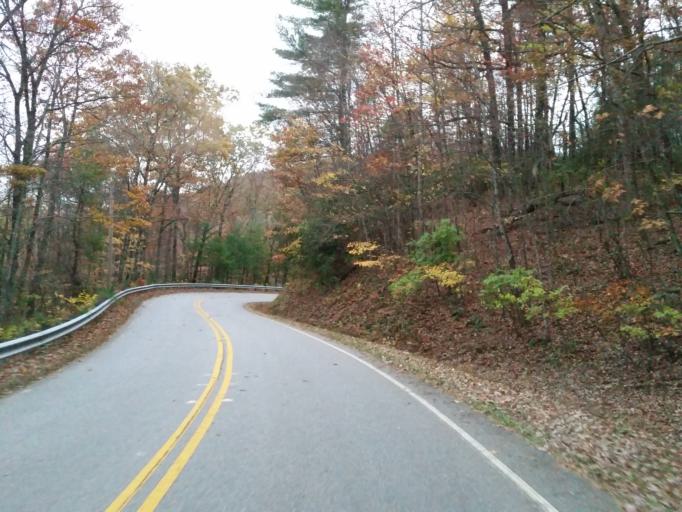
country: US
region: Georgia
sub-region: Lumpkin County
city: Dahlonega
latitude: 34.7038
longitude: -84.0402
